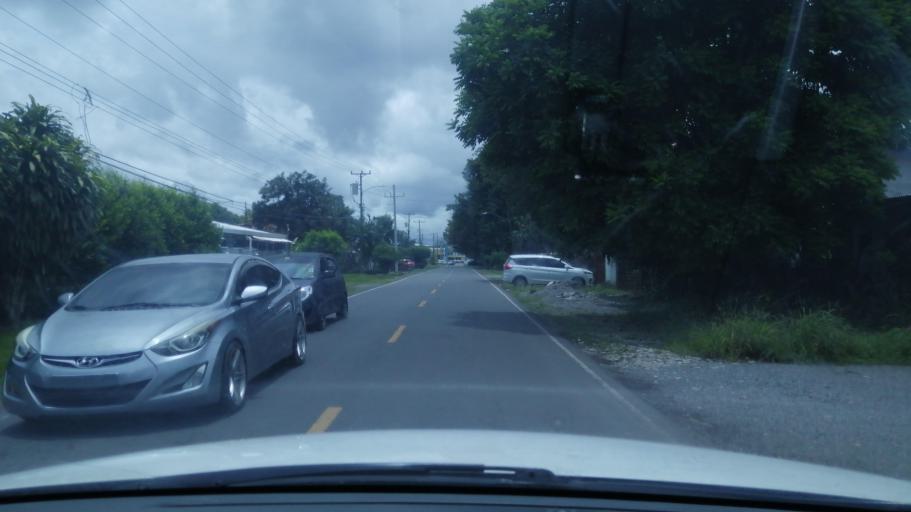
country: PA
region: Chiriqui
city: David
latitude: 8.4407
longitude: -82.4300
